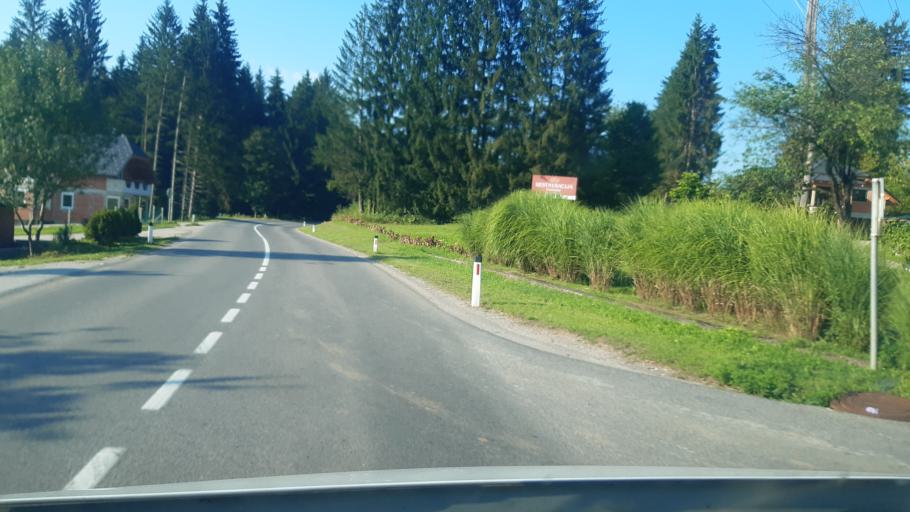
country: SI
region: Crnomelj
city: Crnomelj
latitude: 45.5553
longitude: 15.1662
